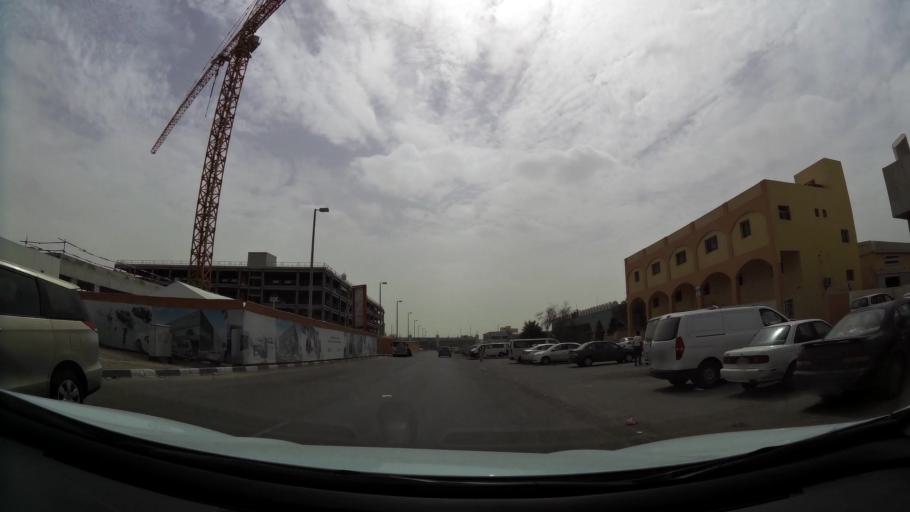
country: AE
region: Abu Dhabi
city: Abu Dhabi
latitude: 24.3716
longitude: 54.5217
